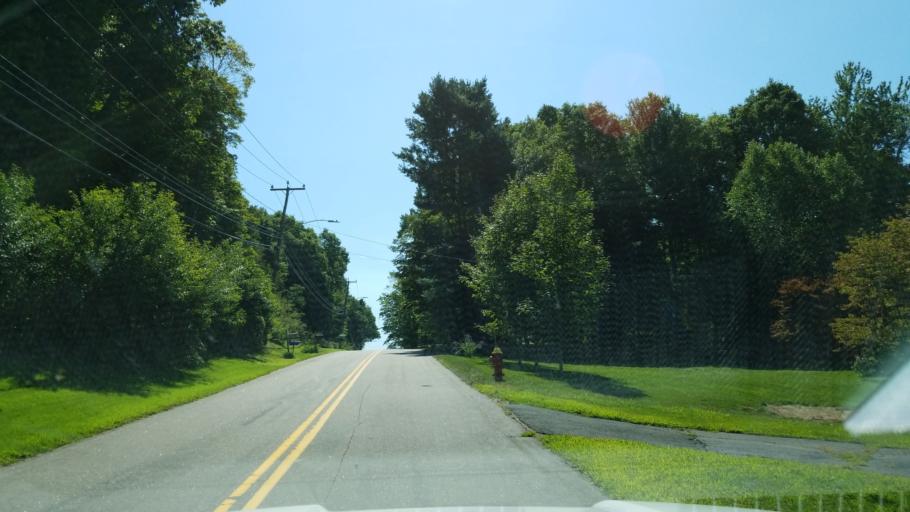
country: US
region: Connecticut
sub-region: Hartford County
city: Tariffville
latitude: 41.8537
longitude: -72.7552
